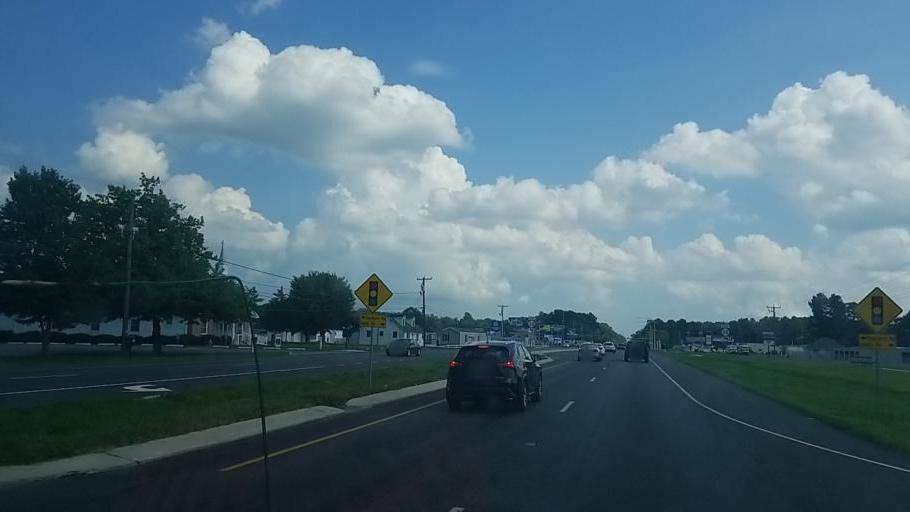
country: US
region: Delaware
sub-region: Sussex County
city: Millsboro
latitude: 38.5696
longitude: -75.2814
